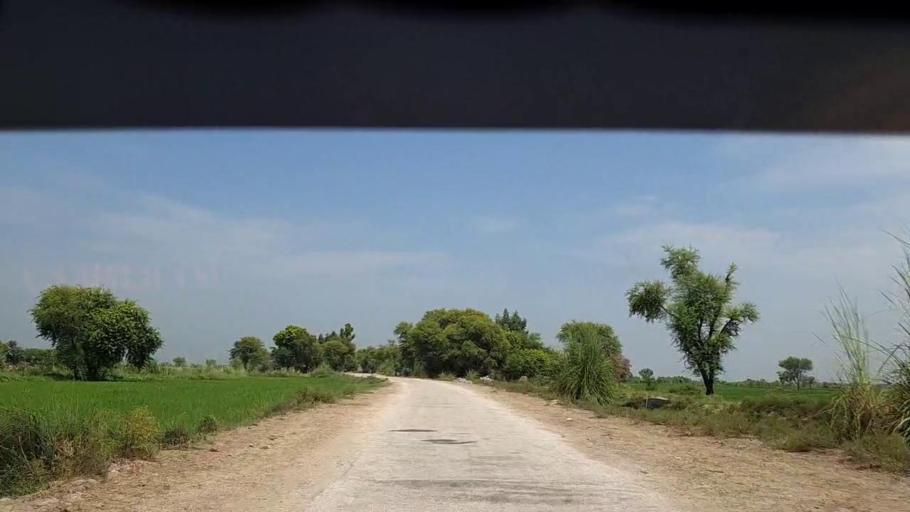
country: PK
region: Sindh
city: Shikarpur
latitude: 28.0663
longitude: 68.7055
